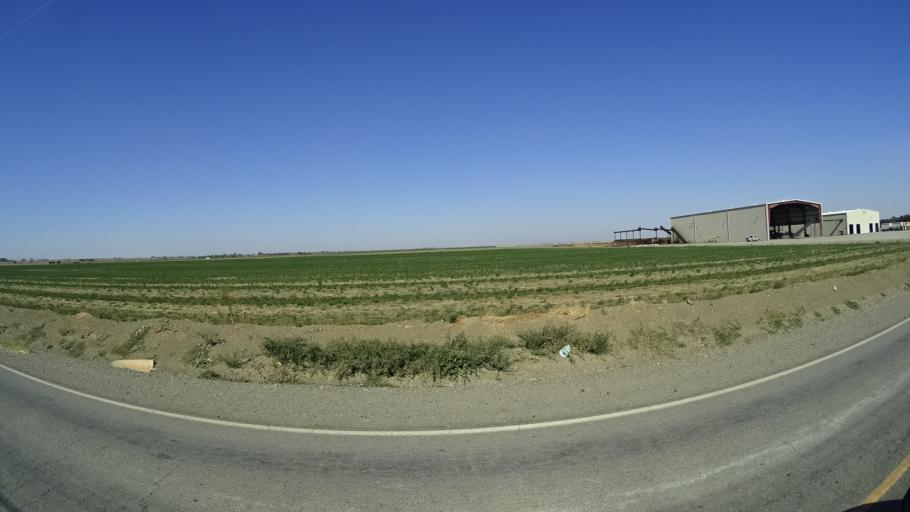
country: US
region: California
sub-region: Yolo County
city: Woodland
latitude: 38.6190
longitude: -121.7512
